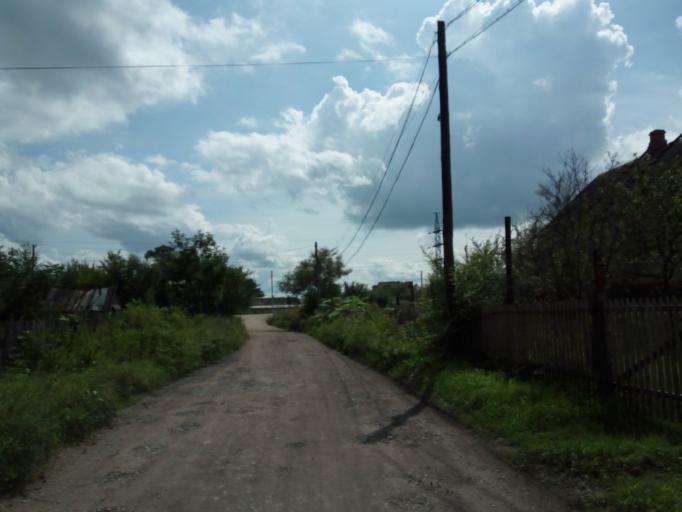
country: RU
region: Primorskiy
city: Dal'nerechensk
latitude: 45.9503
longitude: 133.8174
